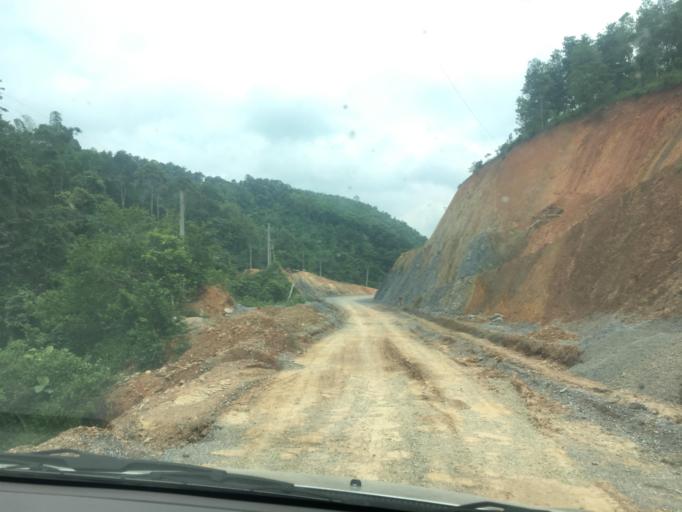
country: VN
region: Bac Kan
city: Yen Lac
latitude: 22.1663
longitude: 106.3015
